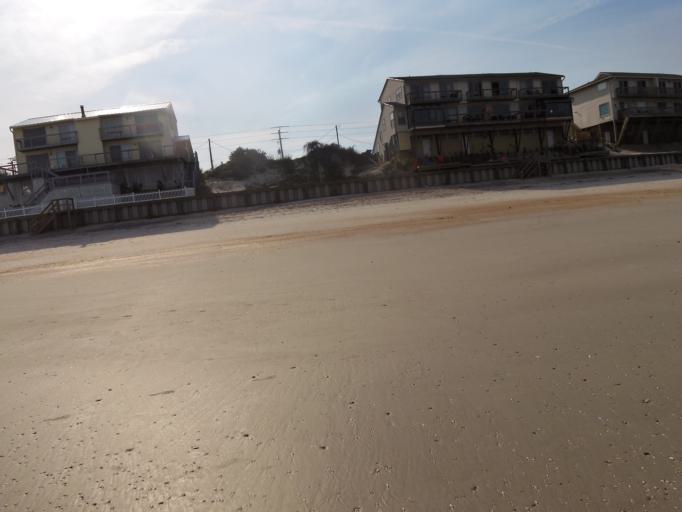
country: US
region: Florida
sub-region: Saint Johns County
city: Villano Beach
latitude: 29.9469
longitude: -81.3019
